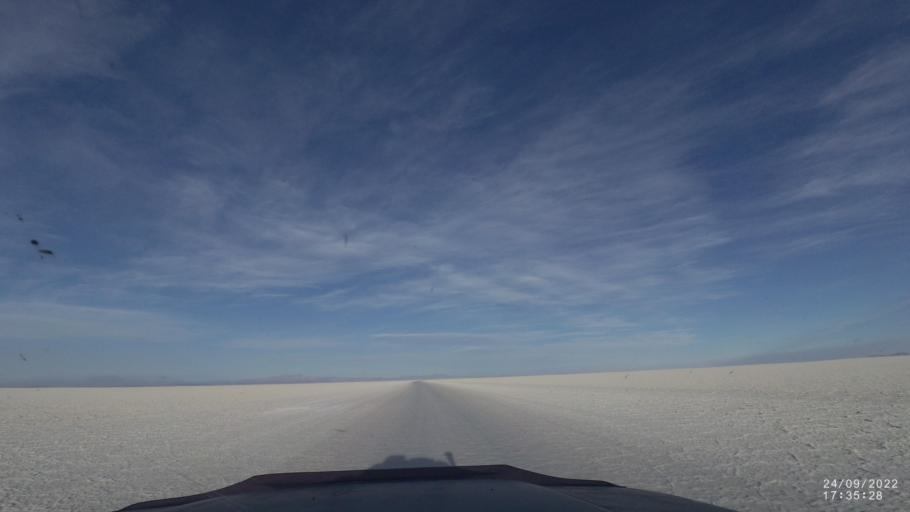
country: BO
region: Potosi
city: Colchani
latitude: -20.3237
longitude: -67.2569
